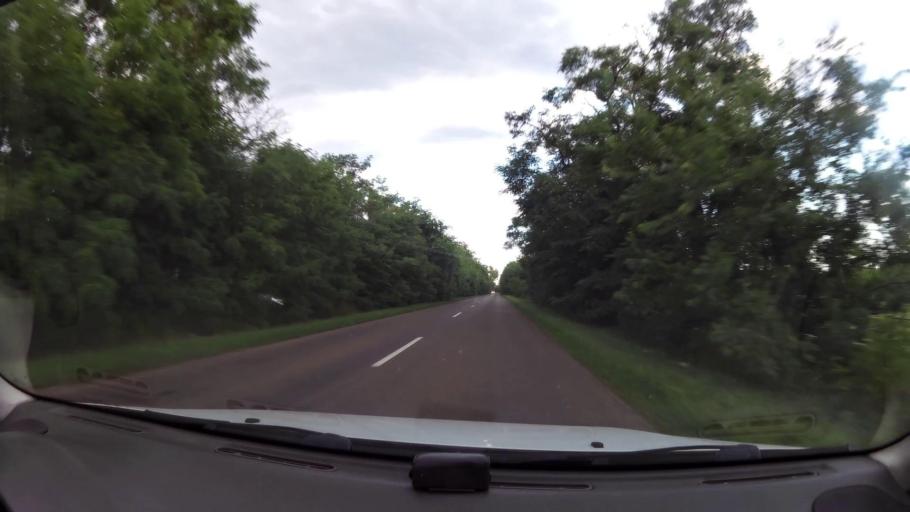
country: HU
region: Pest
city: Tapiosag
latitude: 47.3900
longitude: 19.6454
